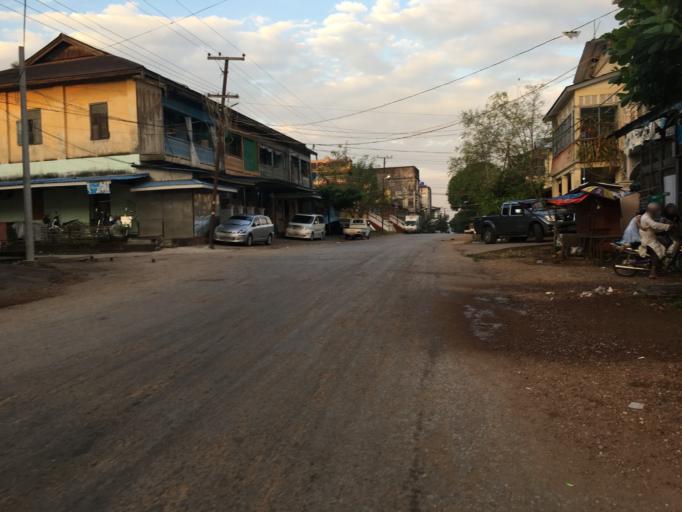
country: MM
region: Mon
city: Mawlamyine
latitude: 16.4859
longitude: 97.6210
